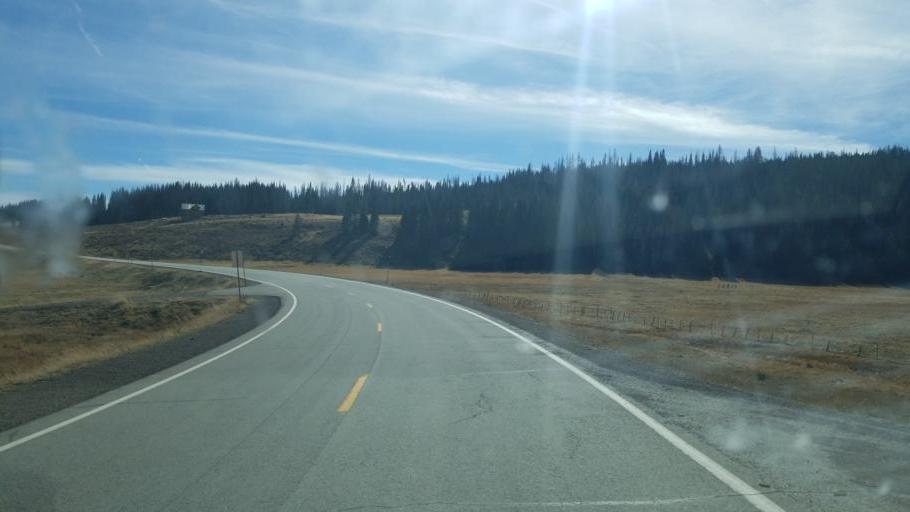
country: US
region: New Mexico
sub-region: Rio Arriba County
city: Chama
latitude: 37.0462
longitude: -106.4115
